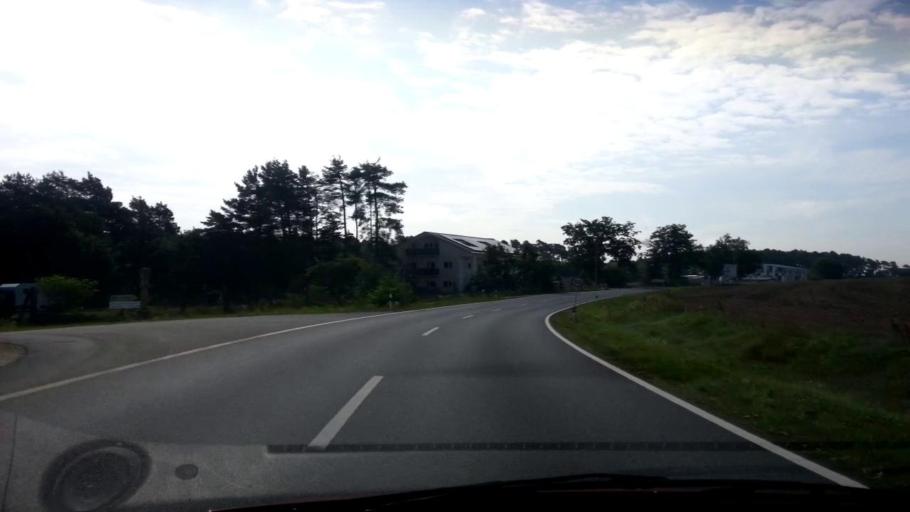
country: DE
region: Bavaria
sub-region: Upper Franconia
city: Hausen
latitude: 49.6954
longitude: 11.0398
